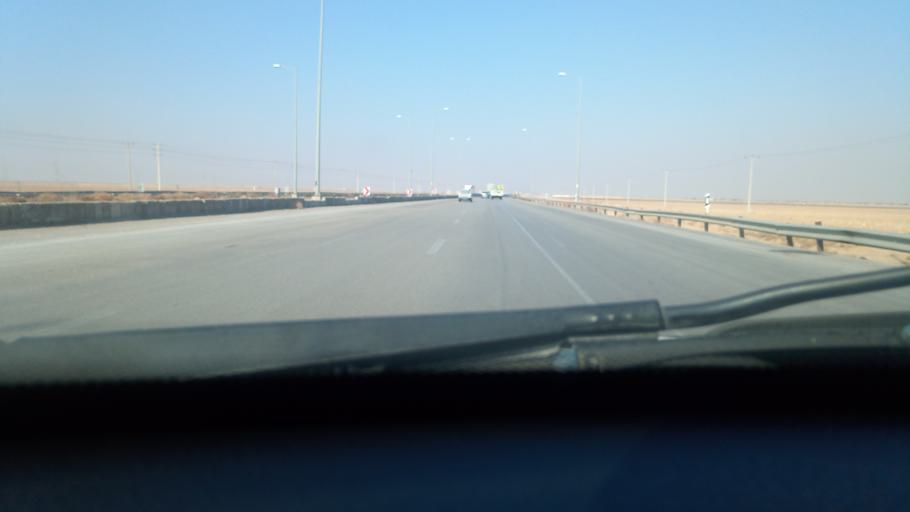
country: IR
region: Razavi Khorasan
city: Chenaran
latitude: 36.7865
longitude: 58.8857
